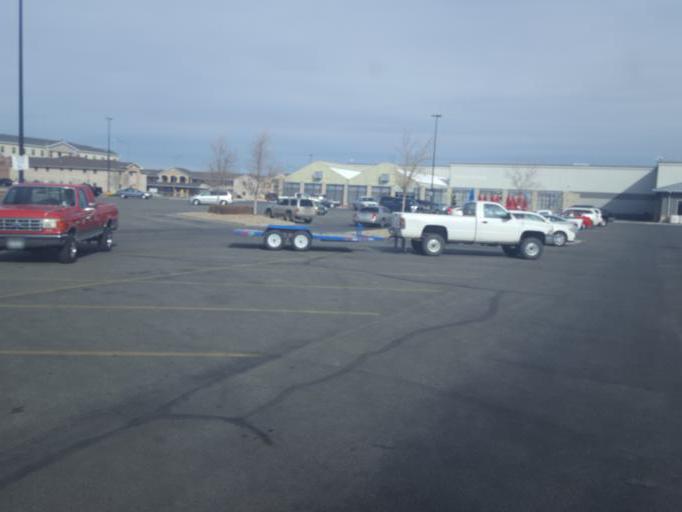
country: US
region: Colorado
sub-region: Alamosa County
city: Alamosa
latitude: 37.4807
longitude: -105.9046
